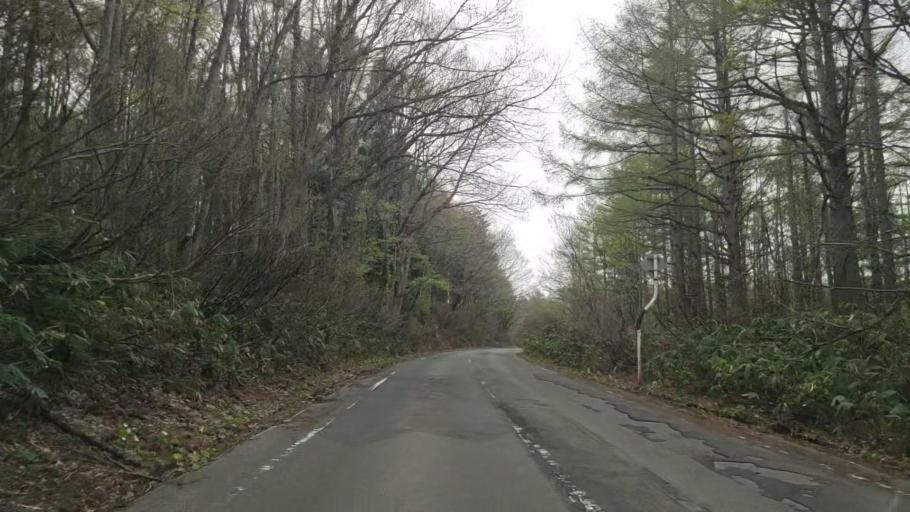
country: JP
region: Aomori
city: Aomori Shi
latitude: 40.7303
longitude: 140.8451
